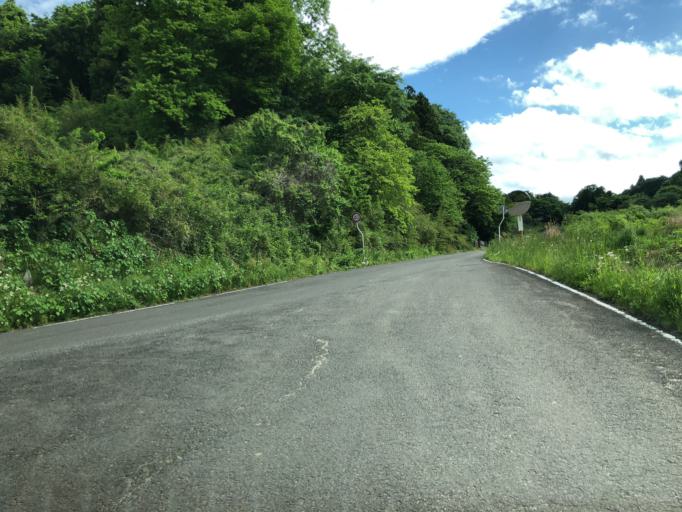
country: JP
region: Fukushima
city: Nihommatsu
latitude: 37.6256
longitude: 140.5129
